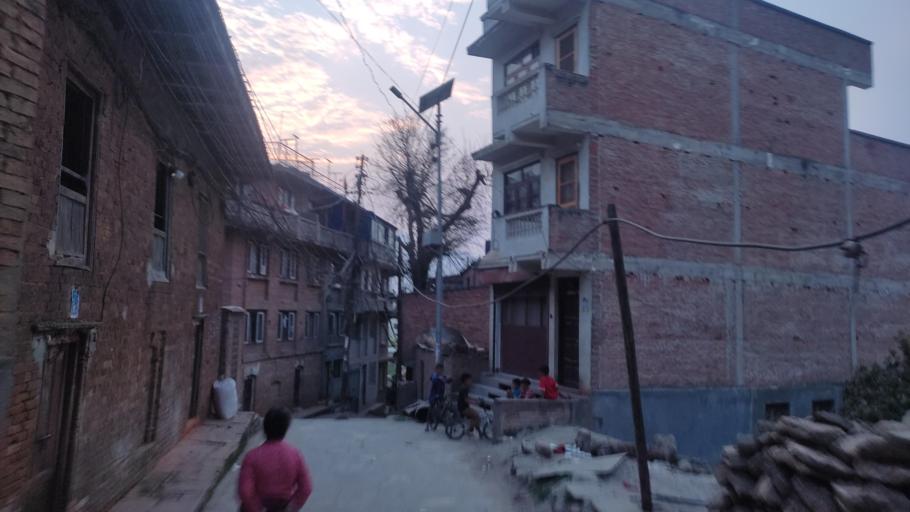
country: NP
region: Central Region
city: Kirtipur
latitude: 27.6697
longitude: 85.2767
